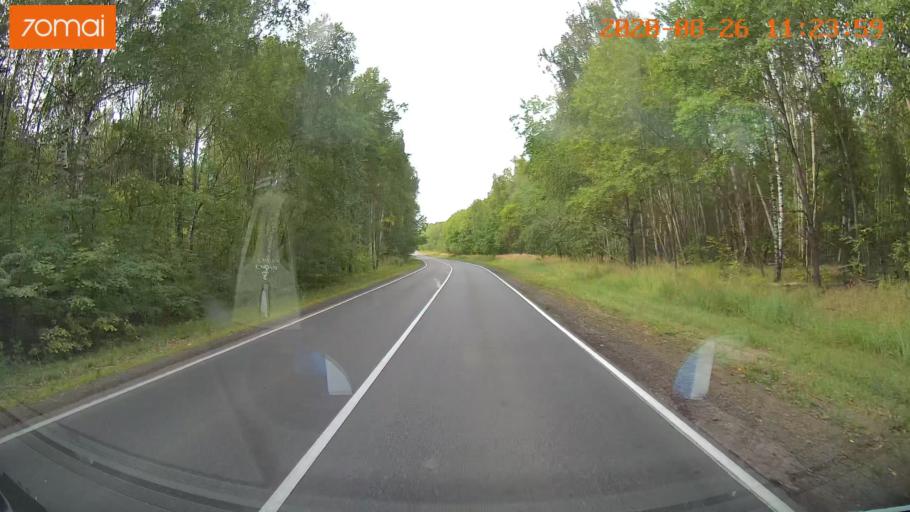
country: RU
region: Rjazan
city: Shilovo
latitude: 54.3489
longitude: 40.9982
